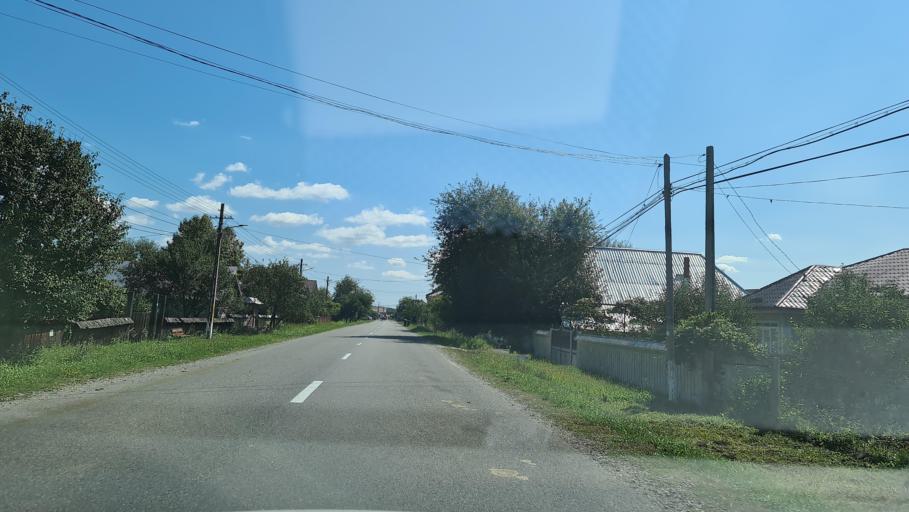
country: RO
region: Bacau
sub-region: Comuna Balcani
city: Balcani
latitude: 46.6485
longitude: 26.5629
